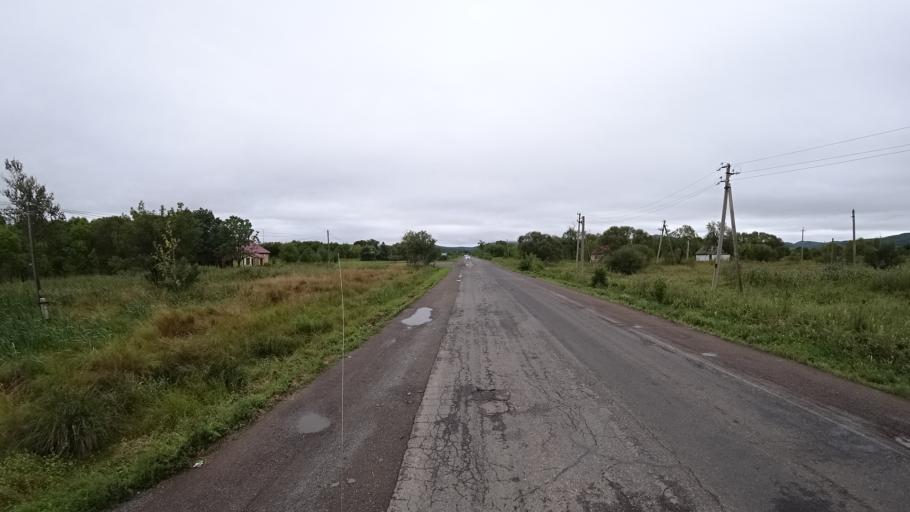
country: RU
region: Primorskiy
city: Monastyrishche
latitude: 44.1953
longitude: 132.4796
